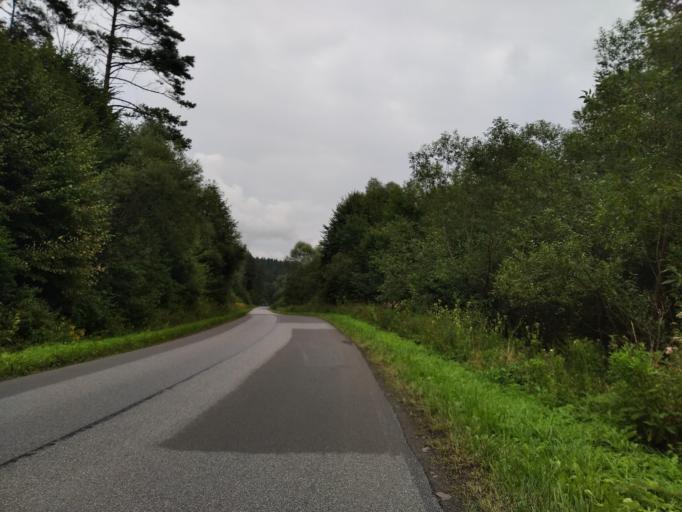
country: PL
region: Subcarpathian Voivodeship
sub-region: Powiat przemyski
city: Bircza
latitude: 49.6915
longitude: 22.4219
